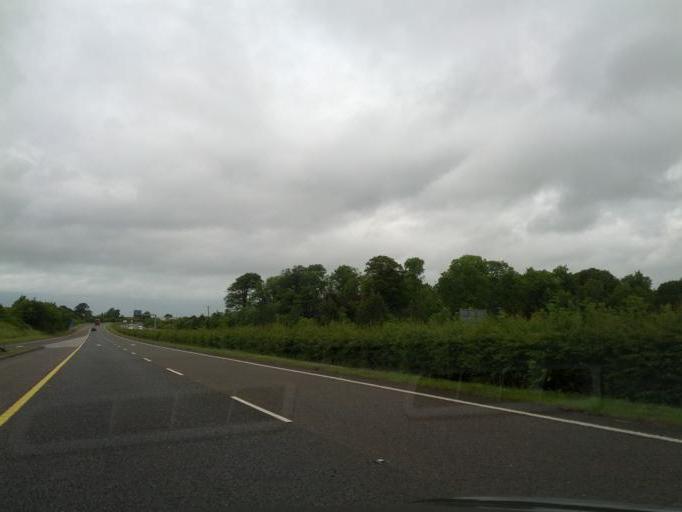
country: IE
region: Munster
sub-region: An Clar
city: Newmarket on Fergus
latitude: 52.7534
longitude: -8.9057
